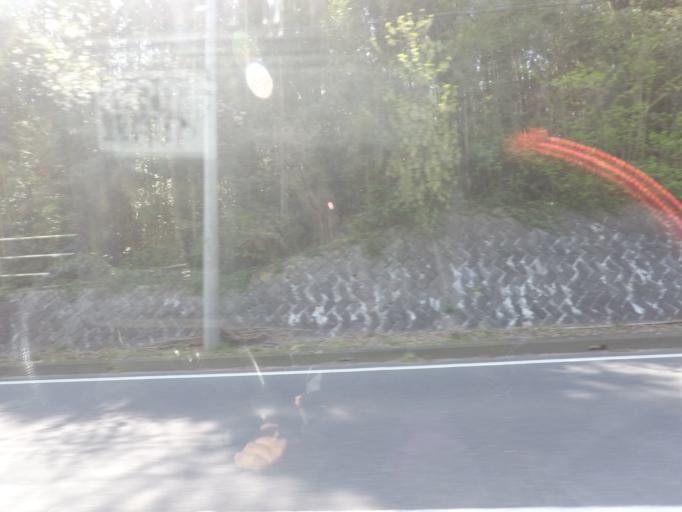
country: JP
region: Chiba
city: Naruto
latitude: 35.6460
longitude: 140.4506
